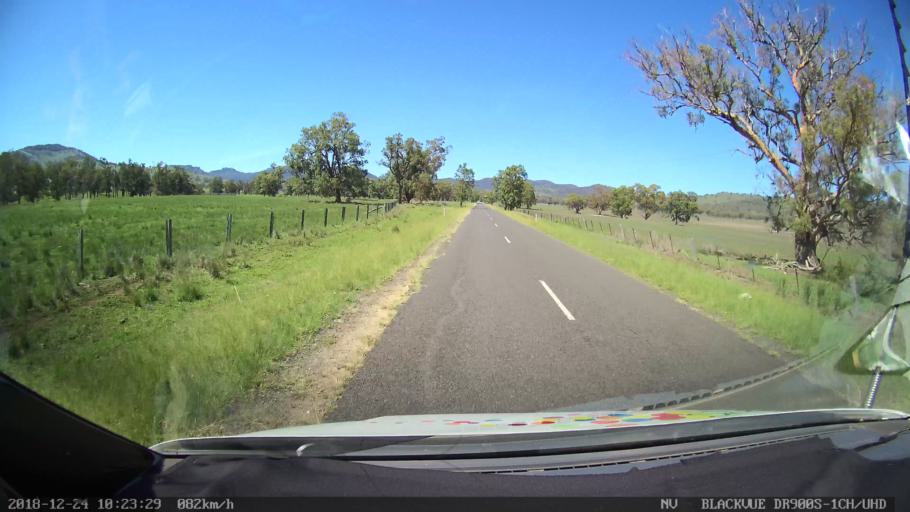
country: AU
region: New South Wales
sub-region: Liverpool Plains
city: Quirindi
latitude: -31.7756
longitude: 150.5377
